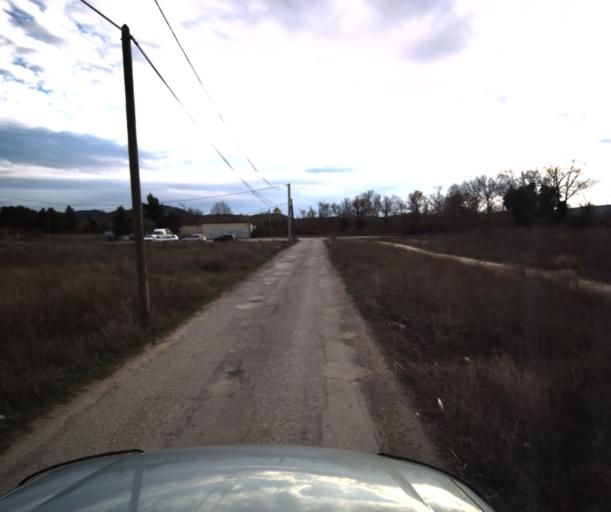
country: FR
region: Provence-Alpes-Cote d'Azur
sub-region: Departement des Bouches-du-Rhone
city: Meyrargues
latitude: 43.6652
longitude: 5.5275
